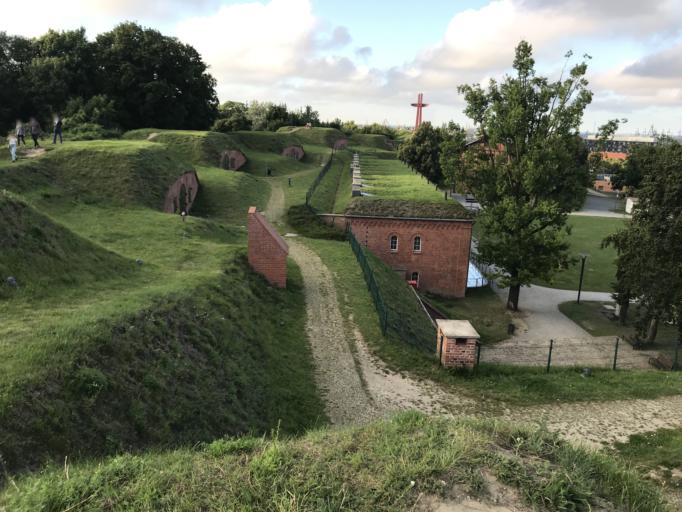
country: PL
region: Pomeranian Voivodeship
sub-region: Gdansk
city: Gdansk
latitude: 54.3559
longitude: 18.6383
